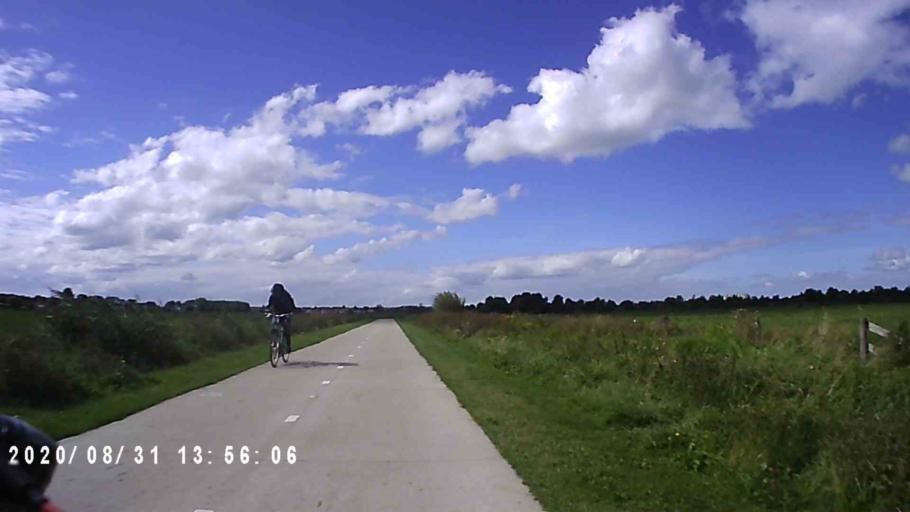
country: NL
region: Groningen
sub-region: Gemeente Groningen
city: Groningen
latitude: 53.2064
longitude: 6.5284
